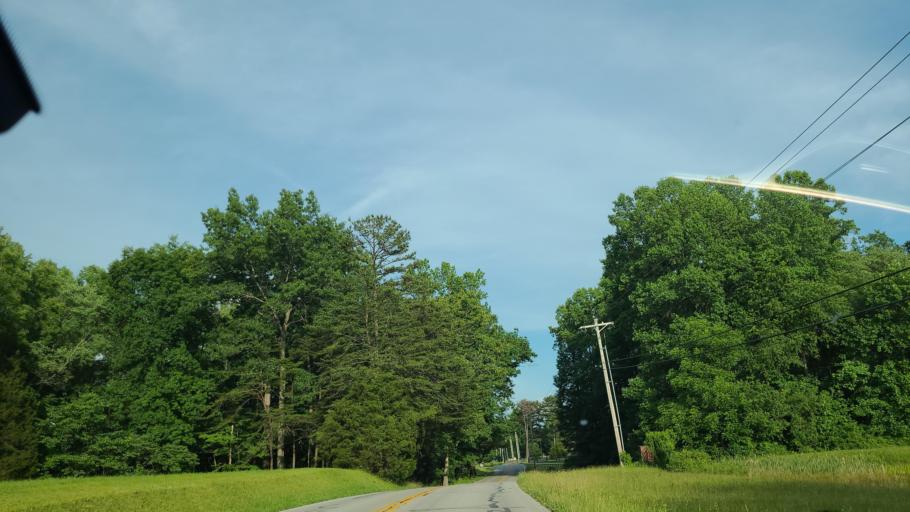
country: US
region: Kentucky
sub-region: Whitley County
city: Corbin
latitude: 36.8937
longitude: -84.2267
